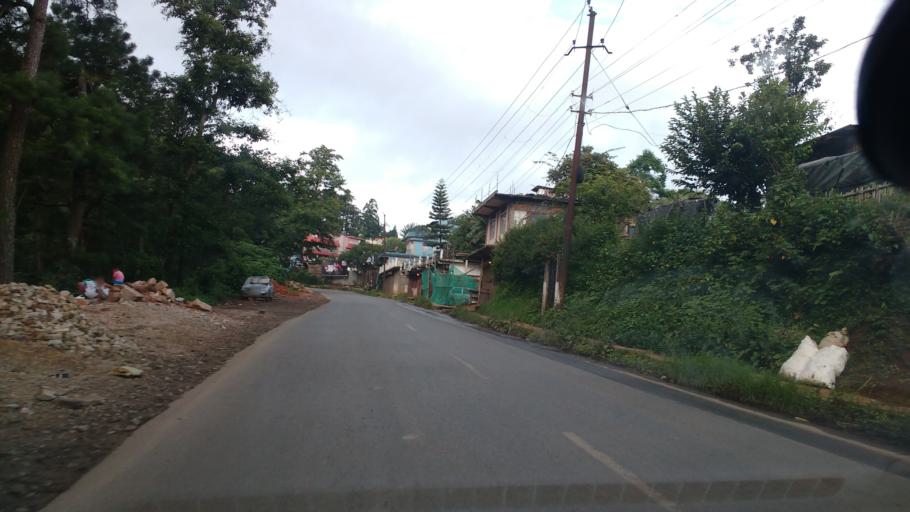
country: IN
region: Meghalaya
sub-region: East Khasi Hills
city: Shillong
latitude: 25.5646
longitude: 91.8549
